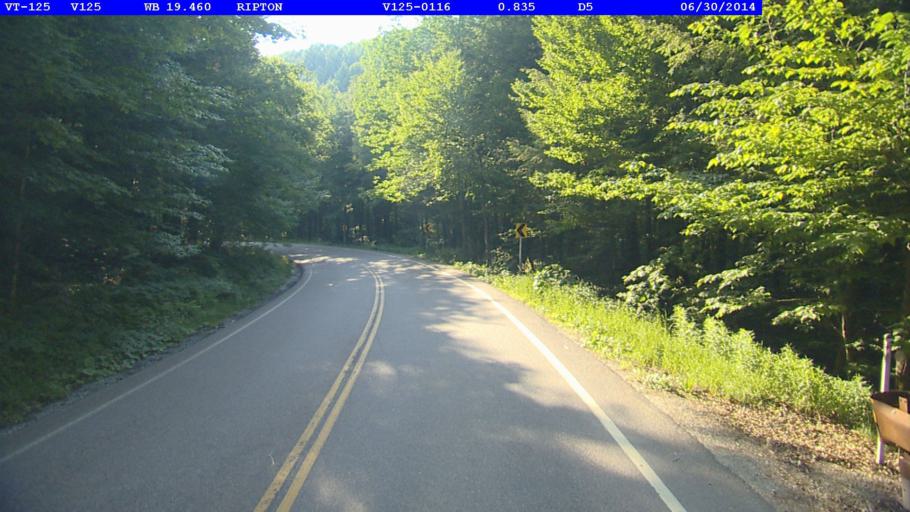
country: US
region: Vermont
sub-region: Addison County
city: Middlebury (village)
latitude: 43.9749
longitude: -73.0446
